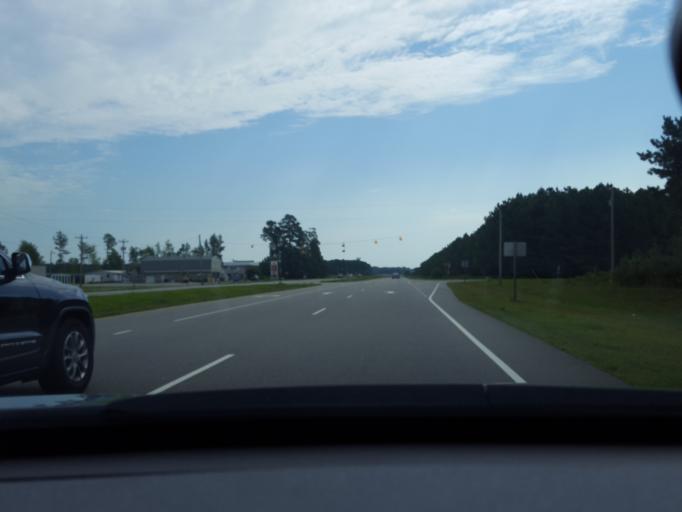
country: US
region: North Carolina
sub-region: Chowan County
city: Edenton
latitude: 36.0382
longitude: -76.7403
